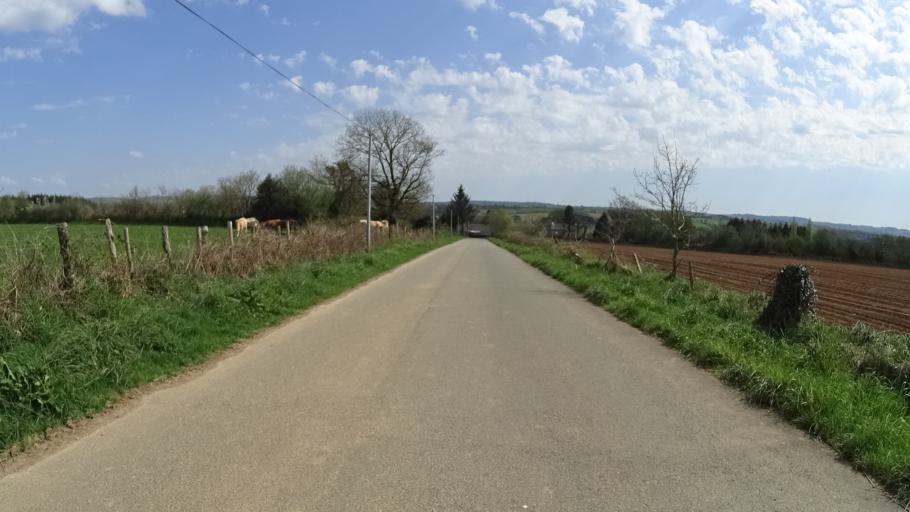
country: FR
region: Brittany
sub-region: Departement du Finistere
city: Sizun
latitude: 48.4278
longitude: -4.0430
